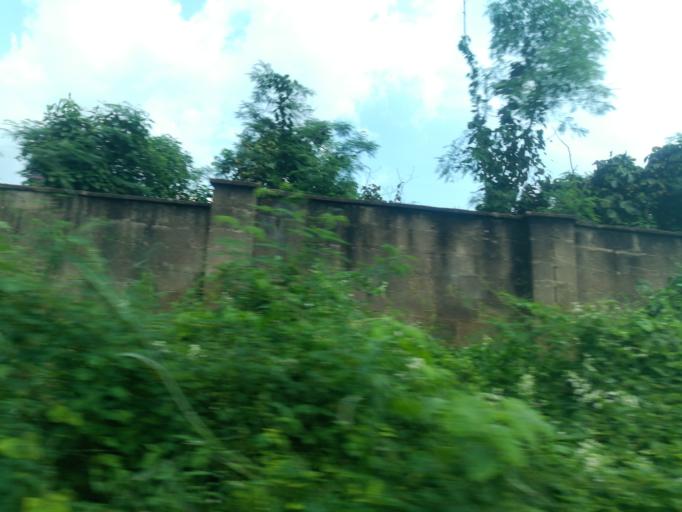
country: NG
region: Oyo
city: Ibadan
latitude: 7.3779
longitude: 3.8359
